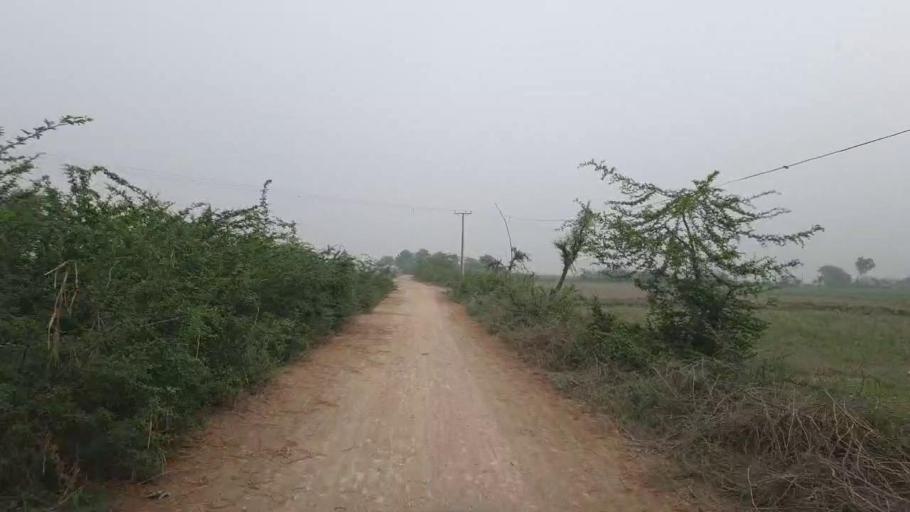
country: PK
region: Sindh
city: Badin
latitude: 24.6290
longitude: 68.7028
